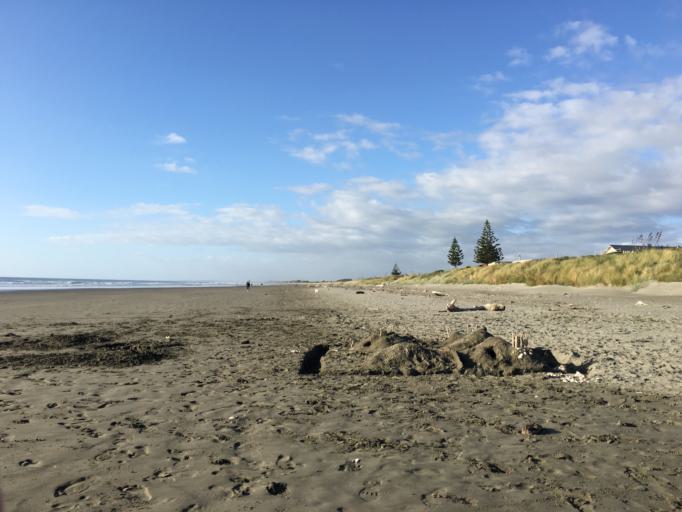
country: NZ
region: Wellington
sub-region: Kapiti Coast District
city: Paraparaumu
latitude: -40.8541
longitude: 175.0319
